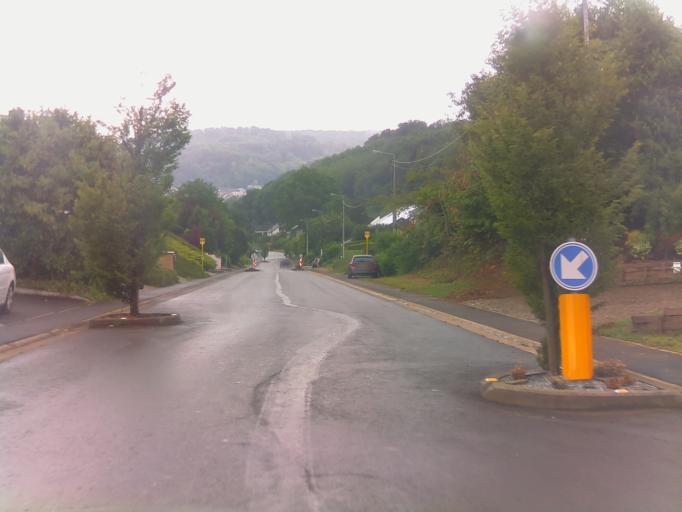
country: BE
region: Wallonia
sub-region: Province du Luxembourg
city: Messancy
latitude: 49.5937
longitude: 5.8345
